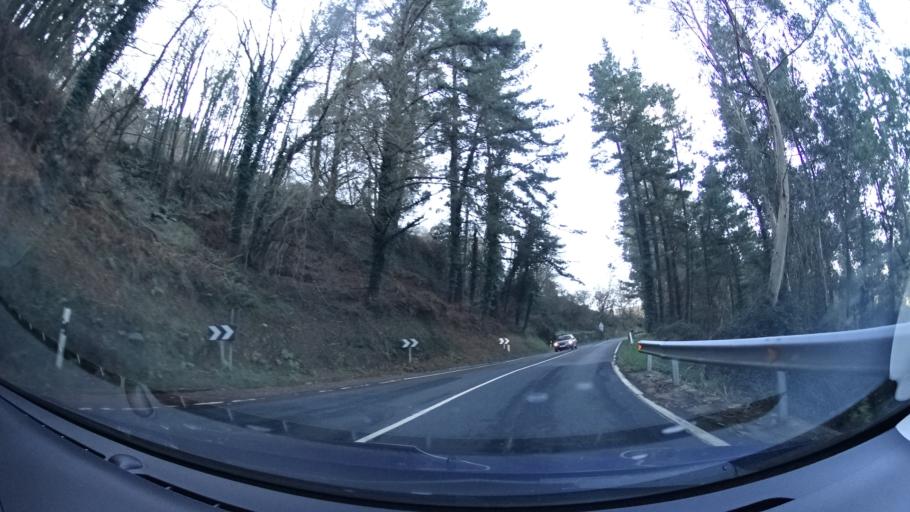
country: ES
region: Basque Country
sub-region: Bizkaia
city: Bermeo
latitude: 43.4084
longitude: -2.7612
